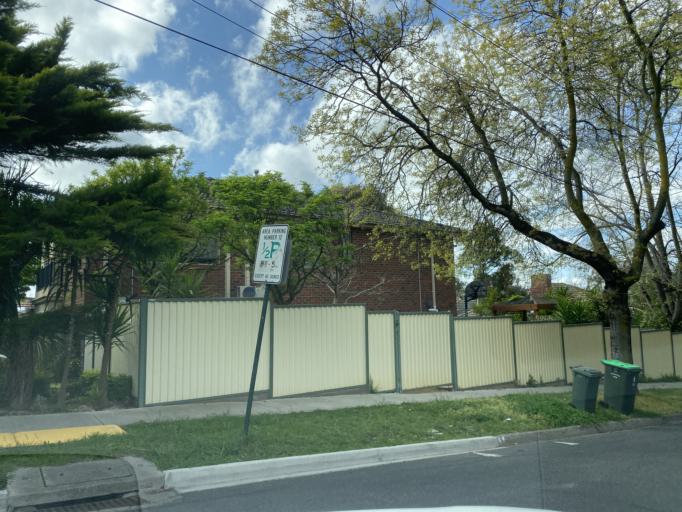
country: AU
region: Victoria
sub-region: Whitehorse
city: Burwood
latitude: -37.8413
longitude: 145.1175
